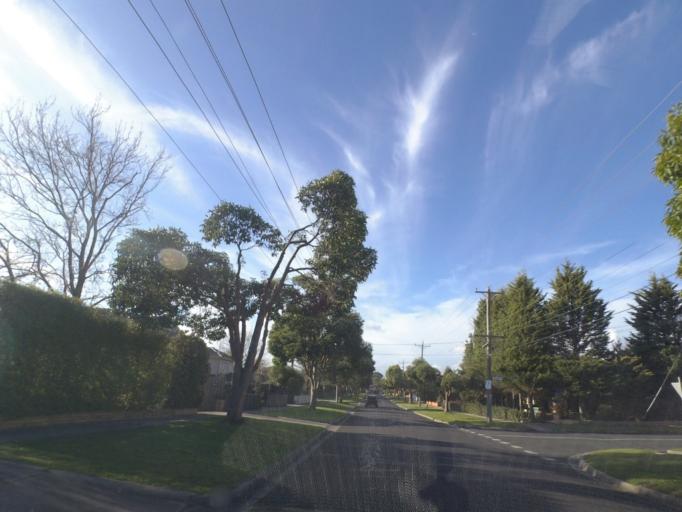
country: AU
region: Victoria
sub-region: Whitehorse
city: Box Hill North
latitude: -37.8015
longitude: 145.1339
